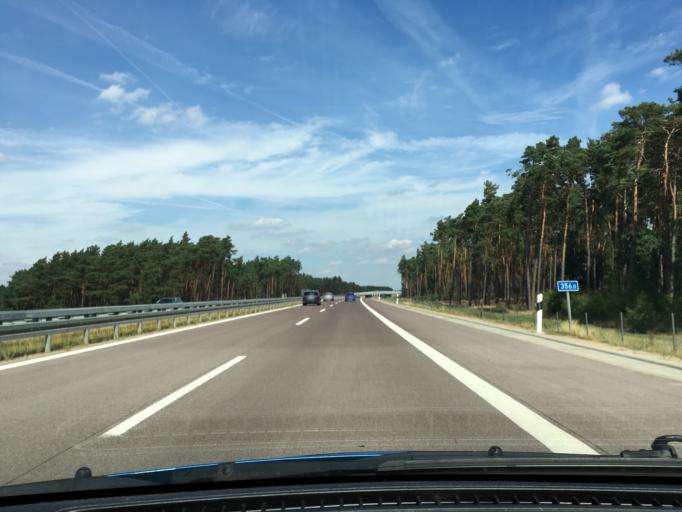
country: DE
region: Mecklenburg-Vorpommern
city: Gross Laasch
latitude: 53.3634
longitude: 11.5159
